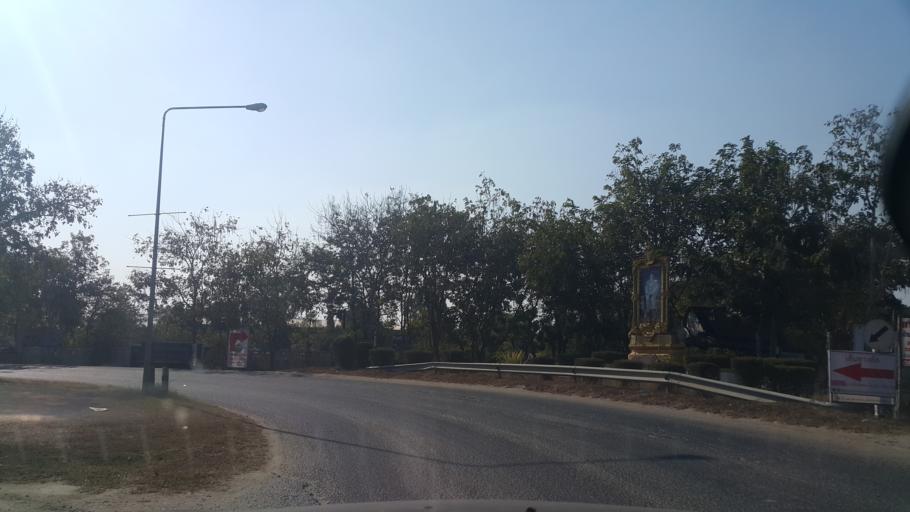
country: TH
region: Nakhon Ratchasima
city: Phimai
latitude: 15.2123
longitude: 102.4462
